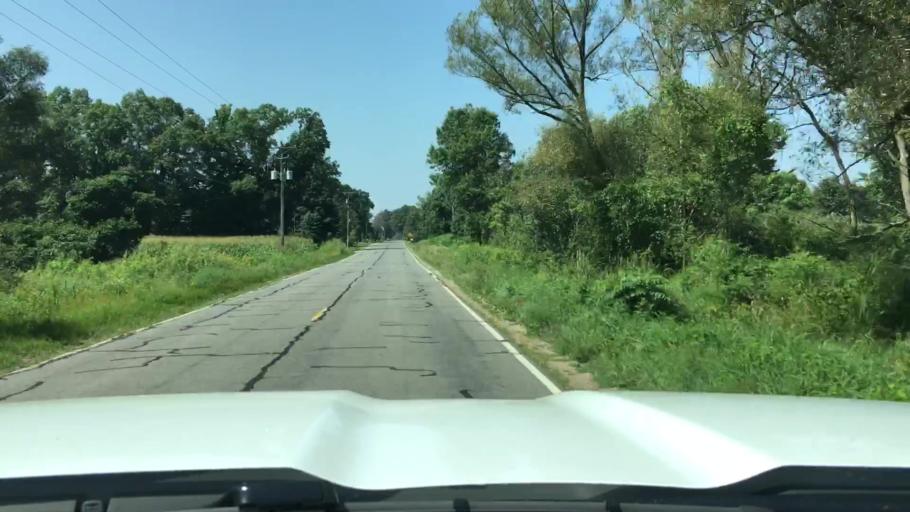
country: US
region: Michigan
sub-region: Saint Joseph County
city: Three Rivers
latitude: 41.9985
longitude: -85.6106
